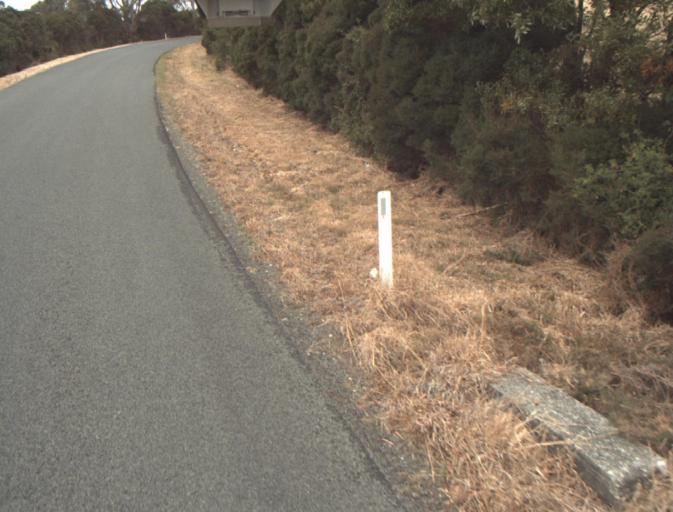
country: AU
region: Tasmania
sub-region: Launceston
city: Mayfield
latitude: -41.2060
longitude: 147.0628
